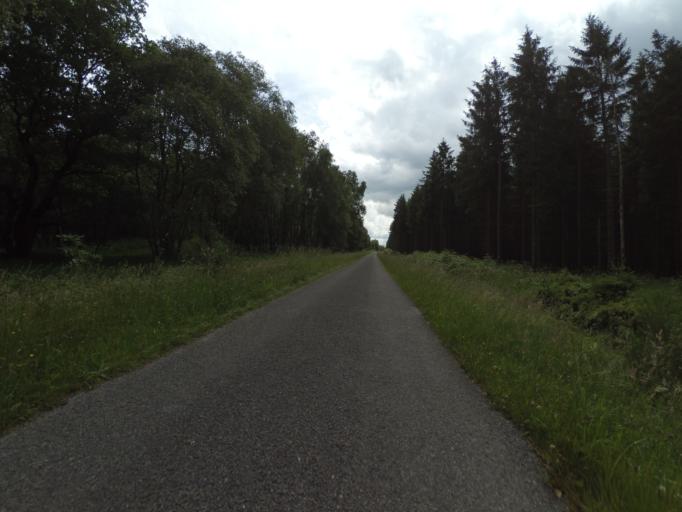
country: DE
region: North Rhine-Westphalia
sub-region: Regierungsbezirk Koln
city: Roetgen
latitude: 50.5904
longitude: 6.1709
